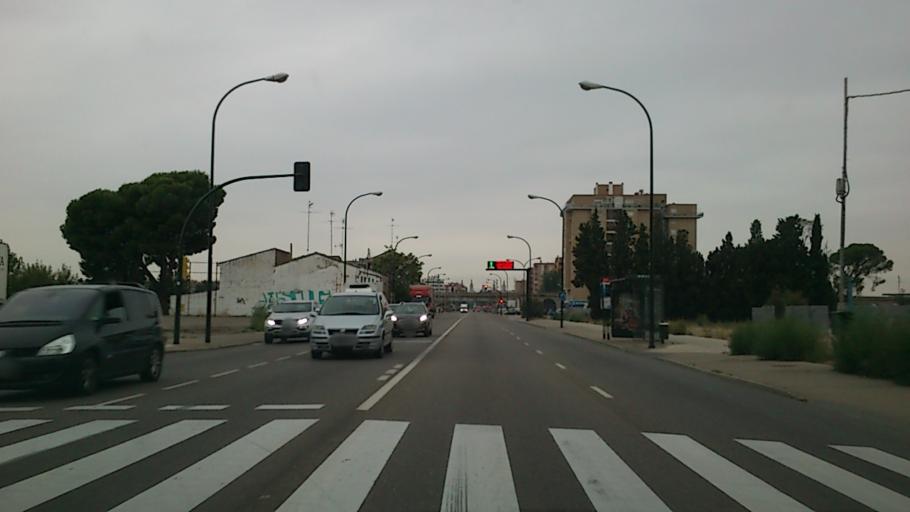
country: ES
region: Aragon
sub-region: Provincia de Zaragoza
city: Zaragoza
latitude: 41.6692
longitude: -0.8483
